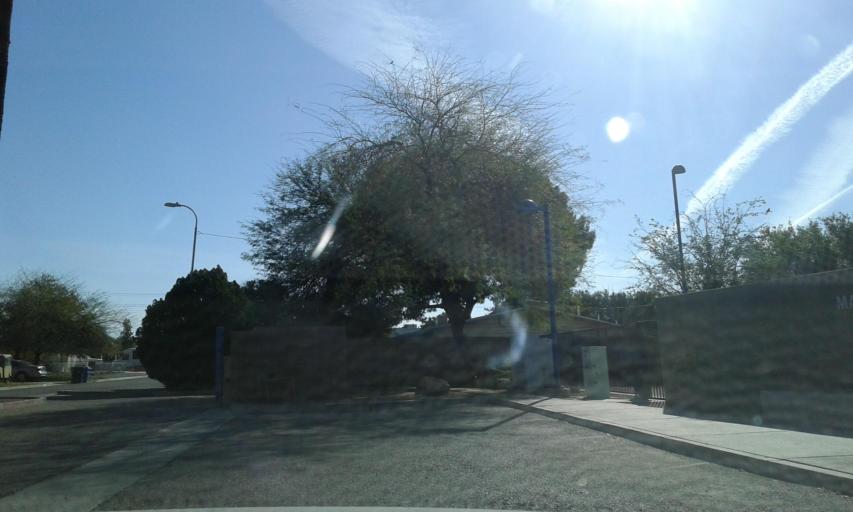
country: US
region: Arizona
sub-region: Maricopa County
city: Phoenix
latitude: 33.5040
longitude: -112.1078
